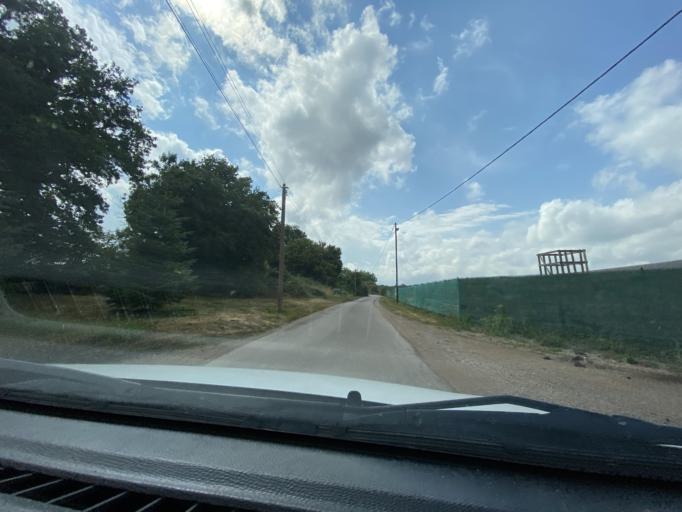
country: FR
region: Bourgogne
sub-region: Departement de la Cote-d'Or
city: Saulieu
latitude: 47.2898
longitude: 4.2372
